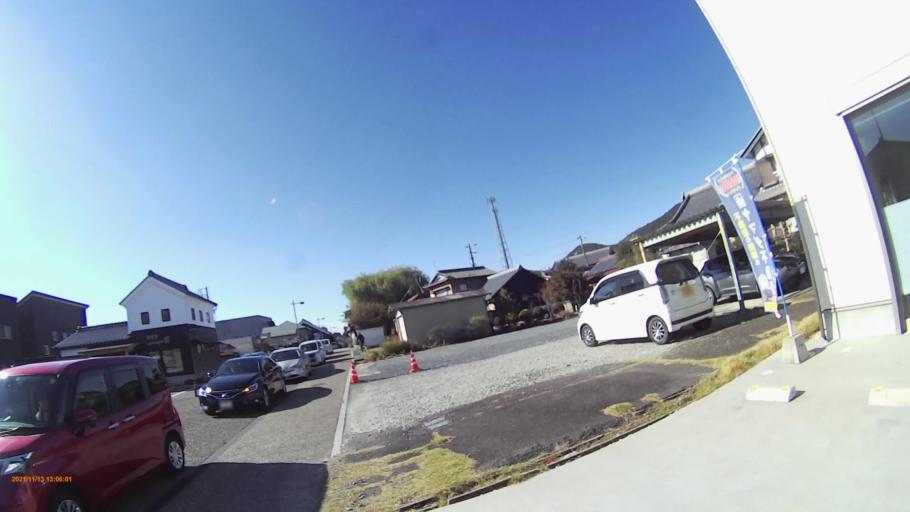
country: JP
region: Gifu
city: Inuyama
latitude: 35.4045
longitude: 136.9383
